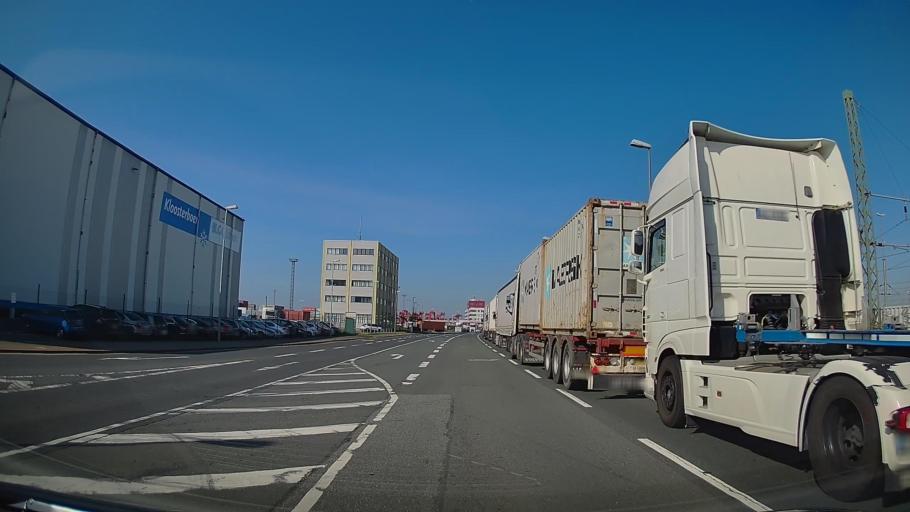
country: DE
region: Bremen
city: Bremerhaven
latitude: 53.5898
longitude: 8.5409
